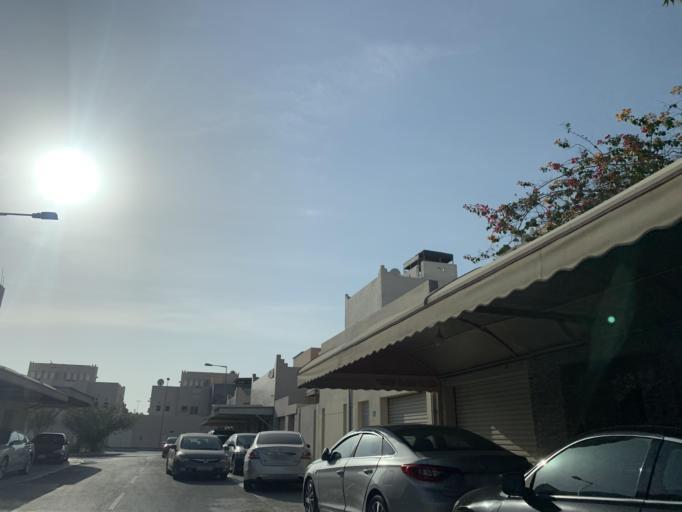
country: BH
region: Central Governorate
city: Madinat Hamad
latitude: 26.1265
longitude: 50.4866
